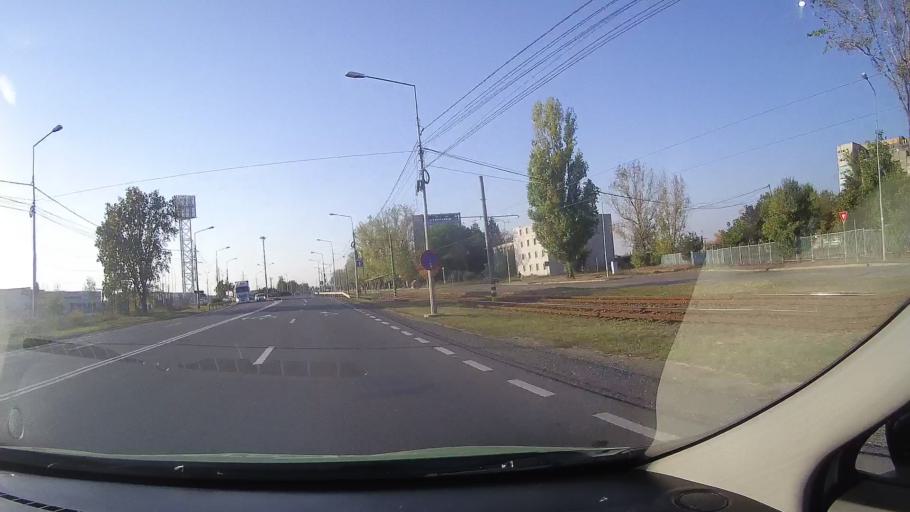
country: RO
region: Bihor
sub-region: Comuna Santandrei
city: Santandrei
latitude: 47.0818
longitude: 21.8907
